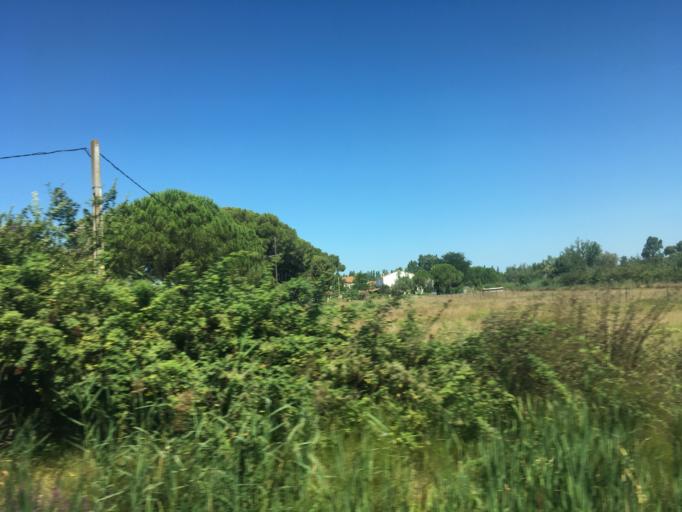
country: FR
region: Languedoc-Roussillon
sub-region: Departement du Gard
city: Saint-Gilles
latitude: 43.5811
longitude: 4.4614
